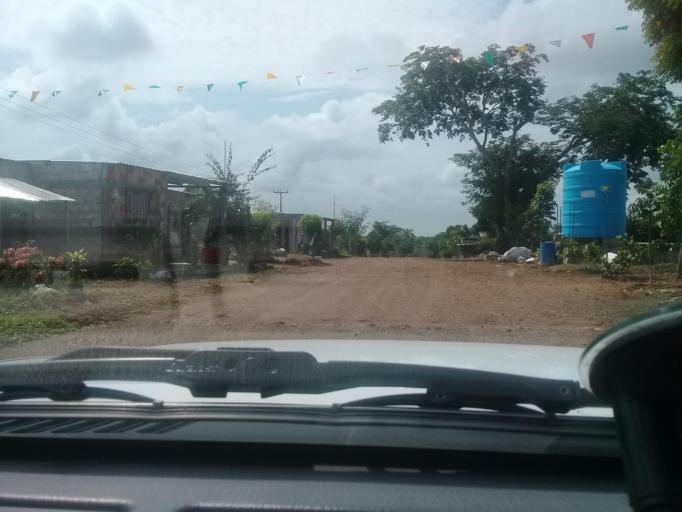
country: MX
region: Veracruz
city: Paso de Ovejas
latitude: 19.2753
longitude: -96.4206
